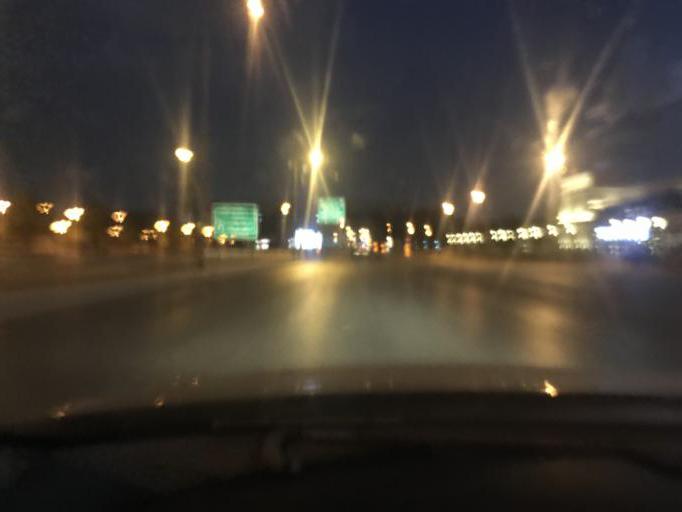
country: SA
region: Ar Riyad
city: Riyadh
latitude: 24.8037
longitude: 46.6948
